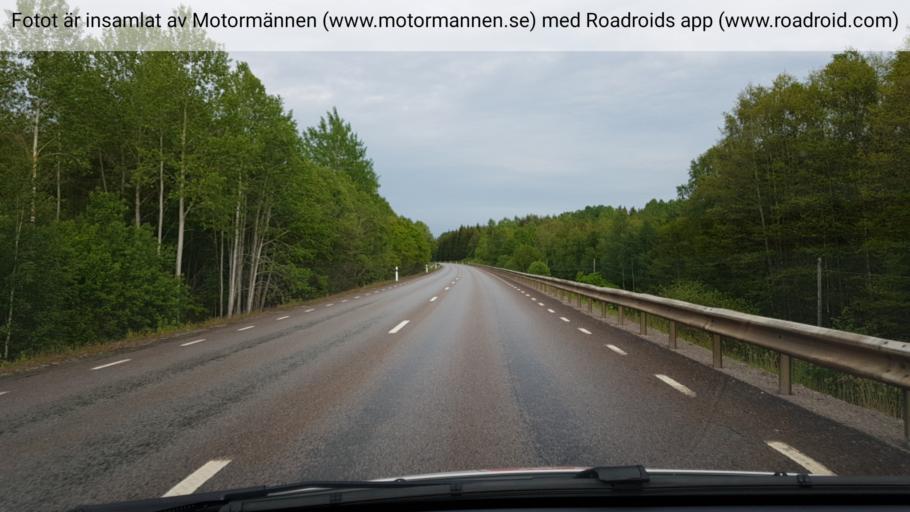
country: SE
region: Kalmar
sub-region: Vasterviks Kommun
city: Ankarsrum
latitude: 57.7102
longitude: 16.1225
